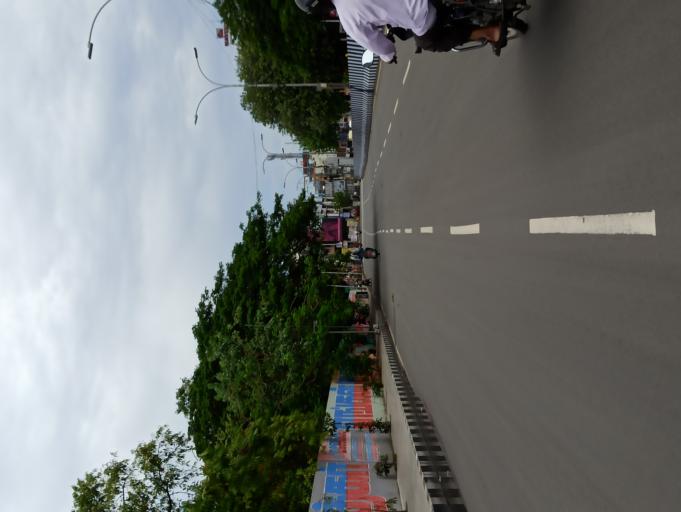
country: IN
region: Tamil Nadu
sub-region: Chennai
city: Gandhi Nagar
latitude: 13.0272
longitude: 80.2343
